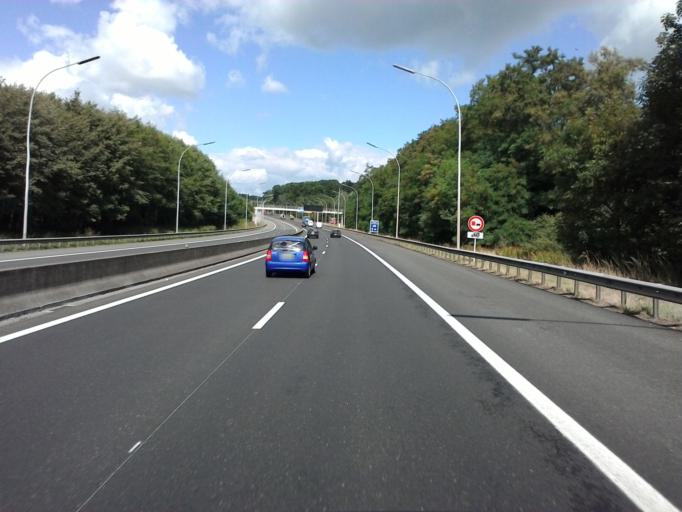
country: LU
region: Luxembourg
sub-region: Canton de Luxembourg
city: Strassen
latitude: 49.6259
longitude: 6.0787
